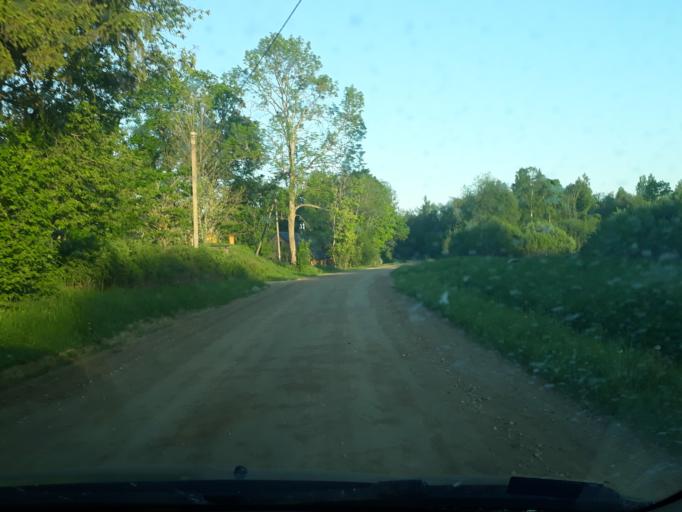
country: EE
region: Paernumaa
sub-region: Vaendra vald (alev)
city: Vandra
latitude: 58.5670
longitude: 24.9475
